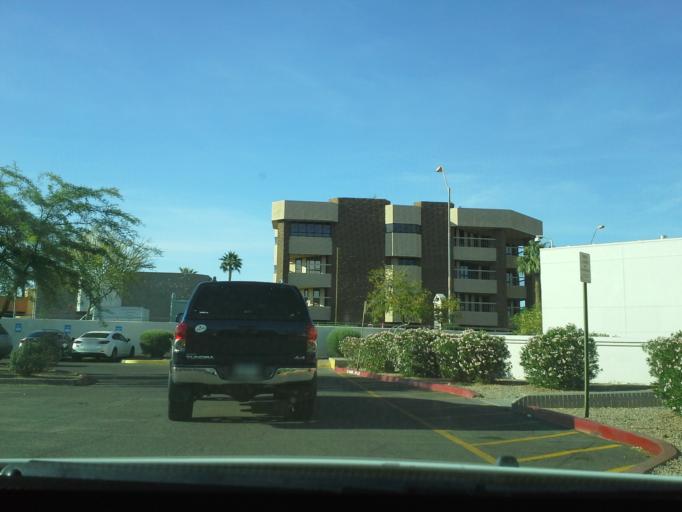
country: US
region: Arizona
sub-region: Maricopa County
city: Phoenix
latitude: 33.4652
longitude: -112.0601
